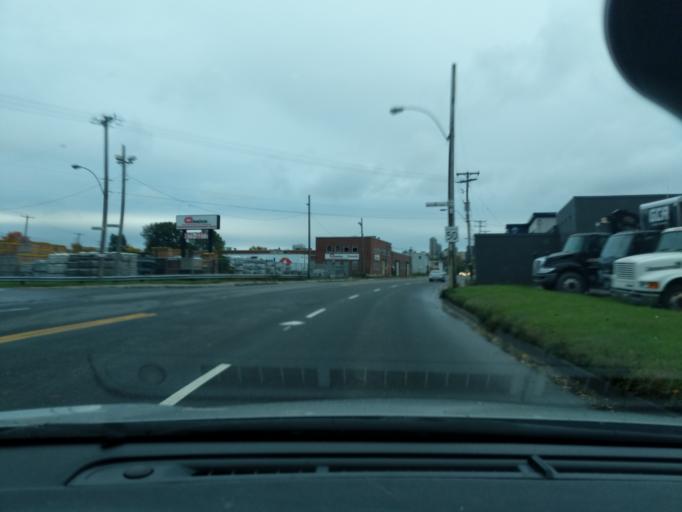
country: CA
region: Quebec
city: Quebec
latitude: 46.8063
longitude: -71.2670
